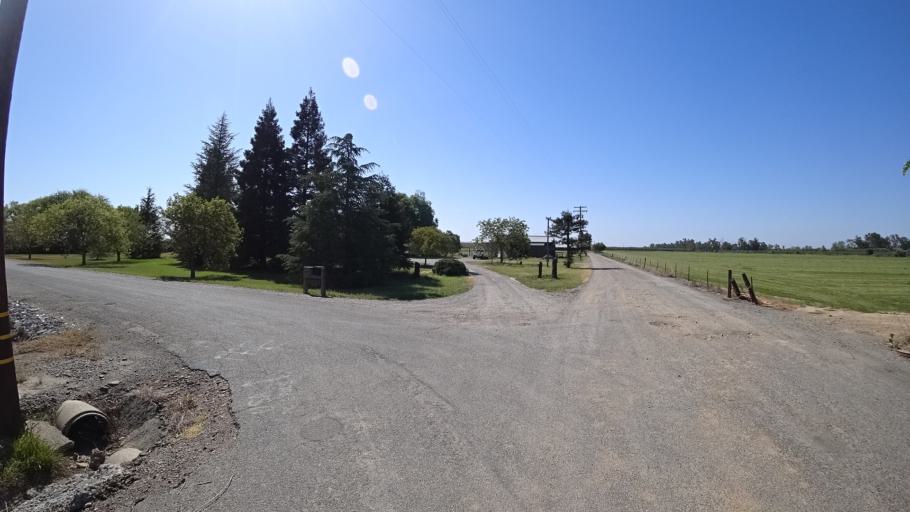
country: US
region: California
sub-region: Glenn County
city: Orland
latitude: 39.7184
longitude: -122.1924
